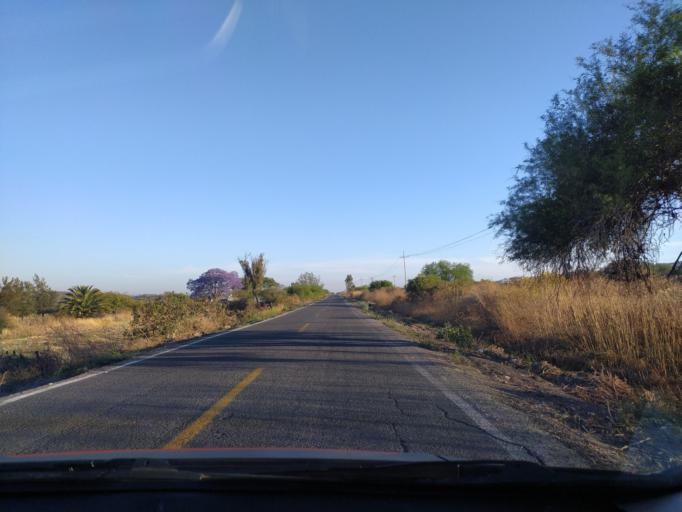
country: MX
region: Guanajuato
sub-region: San Francisco del Rincon
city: San Ignacio de Hidalgo
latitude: 20.8088
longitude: -101.8379
